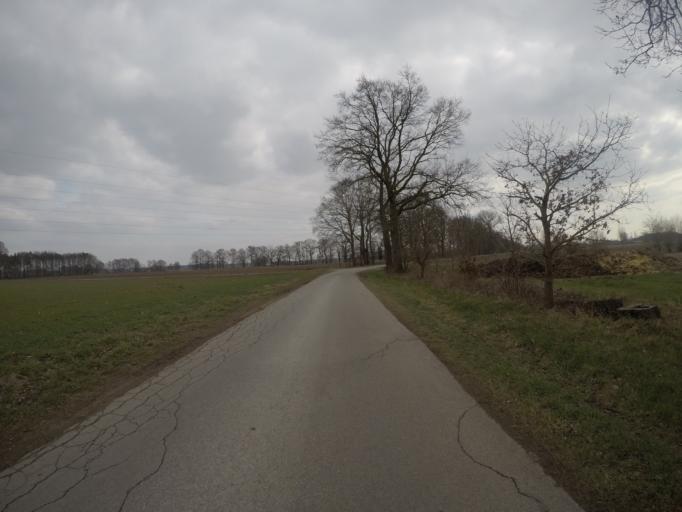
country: DE
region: North Rhine-Westphalia
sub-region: Regierungsbezirk Dusseldorf
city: Hamminkeln
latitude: 51.7849
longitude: 6.5842
